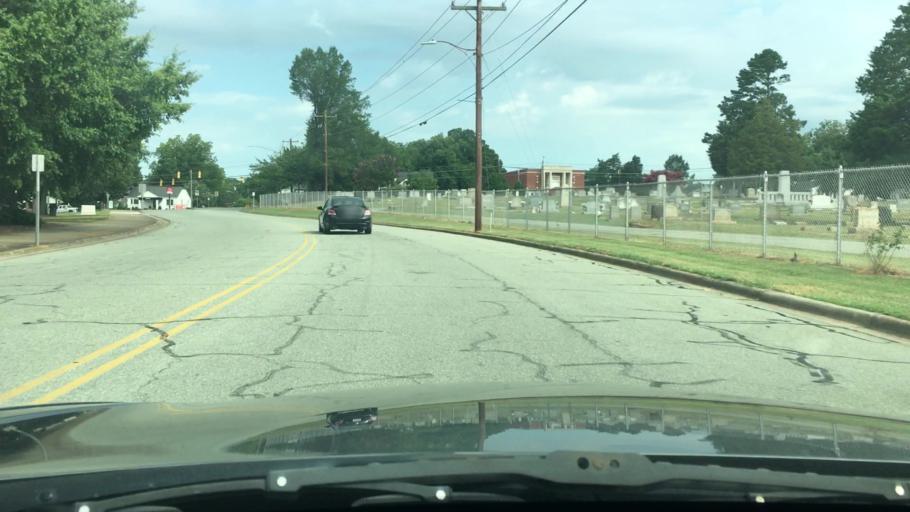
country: US
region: North Carolina
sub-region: Alamance County
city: Burlington
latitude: 36.0843
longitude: -79.4494
